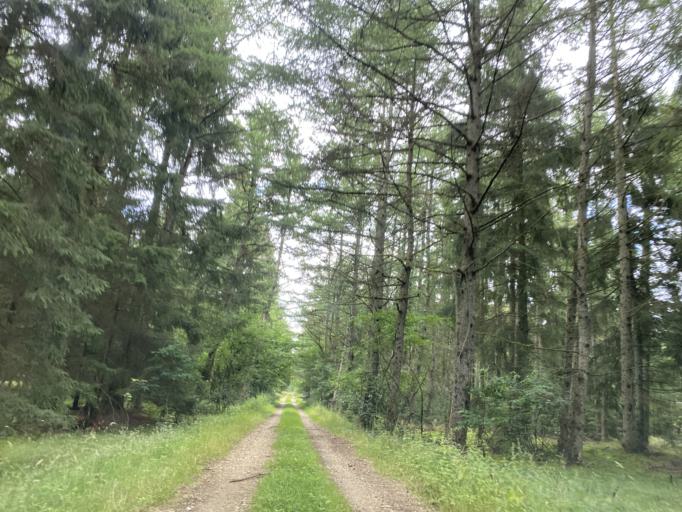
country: DK
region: Central Jutland
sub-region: Viborg Kommune
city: Bjerringbro
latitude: 56.2663
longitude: 9.6476
